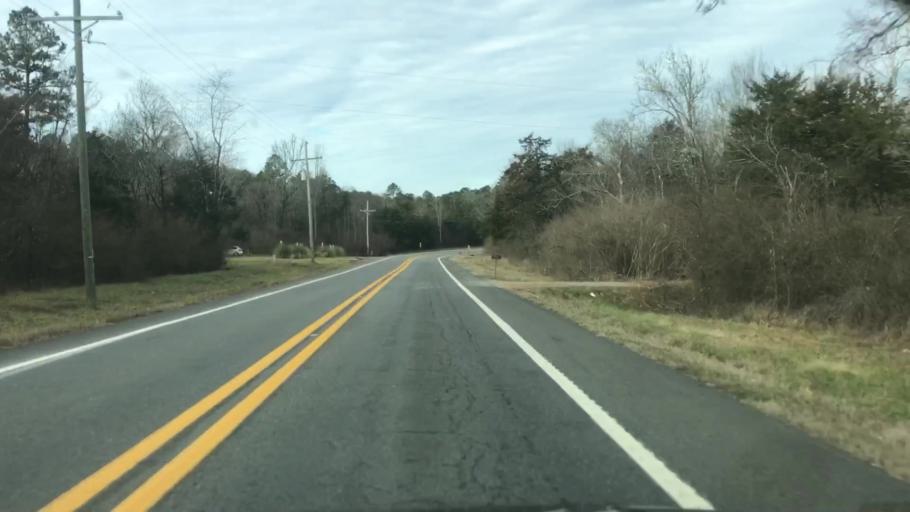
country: US
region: Arkansas
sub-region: Montgomery County
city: Mount Ida
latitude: 34.6084
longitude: -93.6812
